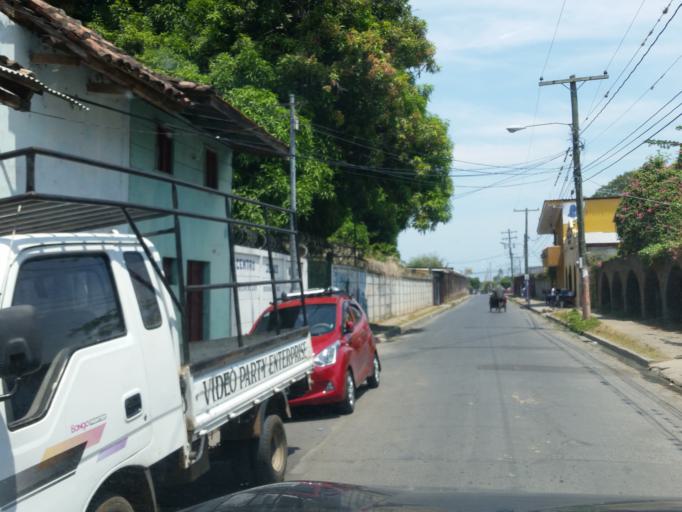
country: NI
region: Granada
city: Granada
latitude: 11.9286
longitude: -85.9489
